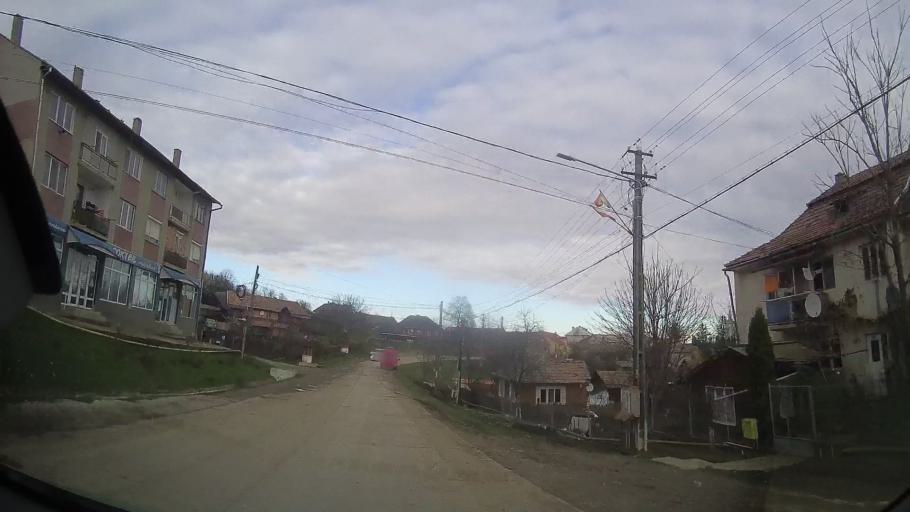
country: RO
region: Bistrita-Nasaud
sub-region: Comuna Sanmihaiu de Campie
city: Sanmihaiu de Campie
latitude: 46.8925
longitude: 24.3311
